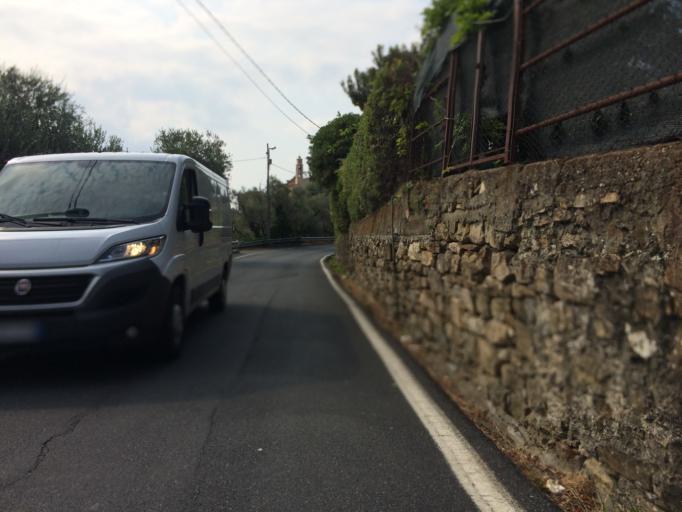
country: IT
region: Liguria
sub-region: Provincia di Imperia
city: San Remo
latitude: 43.8358
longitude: 7.7582
